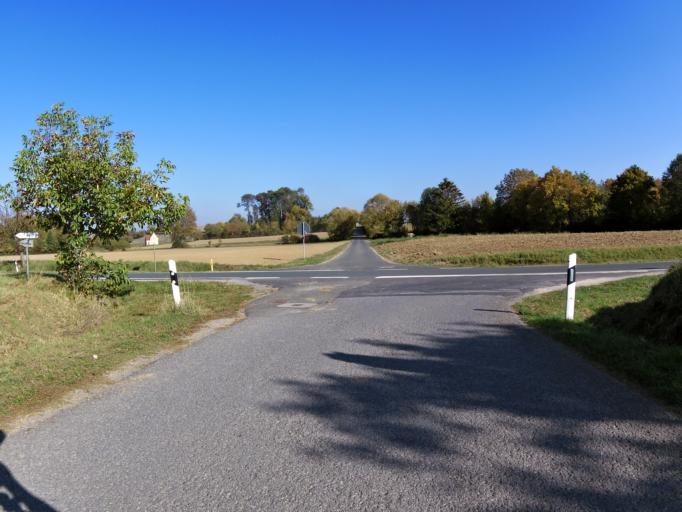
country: DE
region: Bavaria
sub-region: Regierungsbezirk Unterfranken
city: Geroldshausen
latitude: 49.6971
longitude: 9.9252
